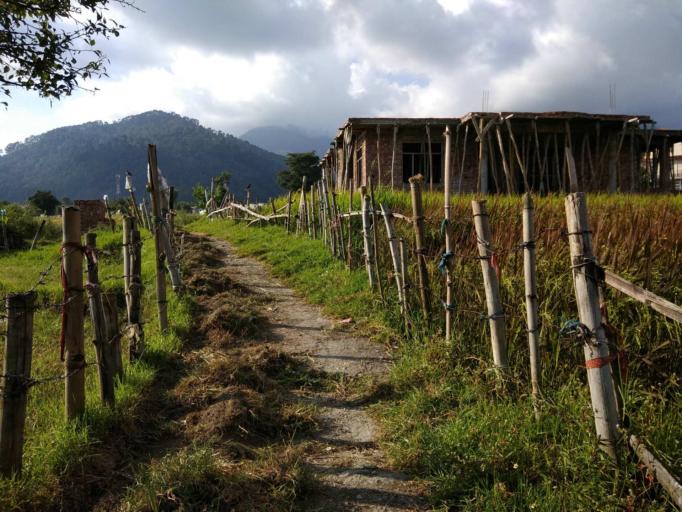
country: IN
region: Himachal Pradesh
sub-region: Kangra
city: Palampur
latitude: 32.1250
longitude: 76.5400
